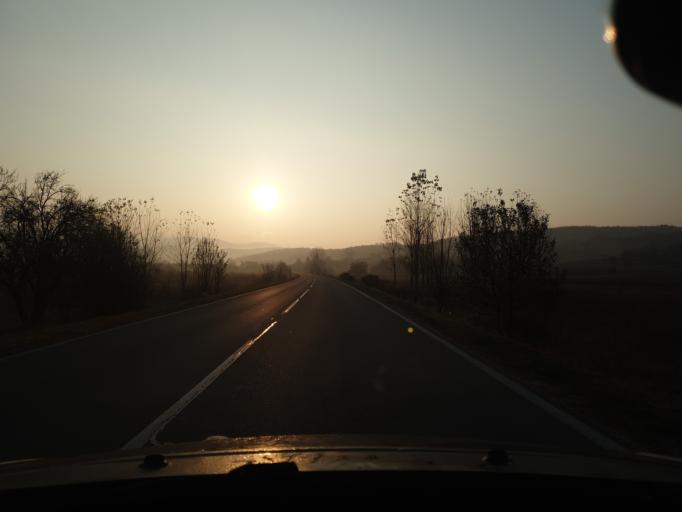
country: RS
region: Central Serbia
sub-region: Jablanicki Okrug
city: Leskovac
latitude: 42.9186
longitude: 22.0263
